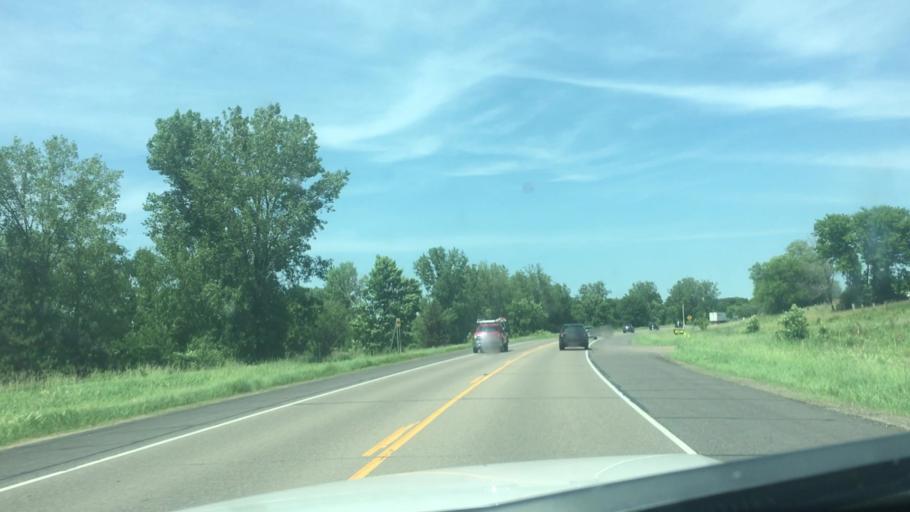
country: US
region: Minnesota
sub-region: Ramsey County
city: White Bear Lake
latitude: 45.1176
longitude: -93.0027
